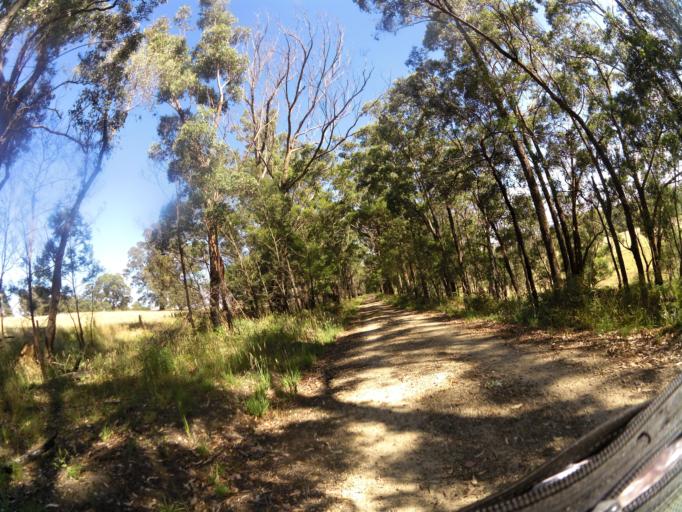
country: AU
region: Victoria
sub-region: East Gippsland
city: Lakes Entrance
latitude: -37.7449
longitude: 148.1745
